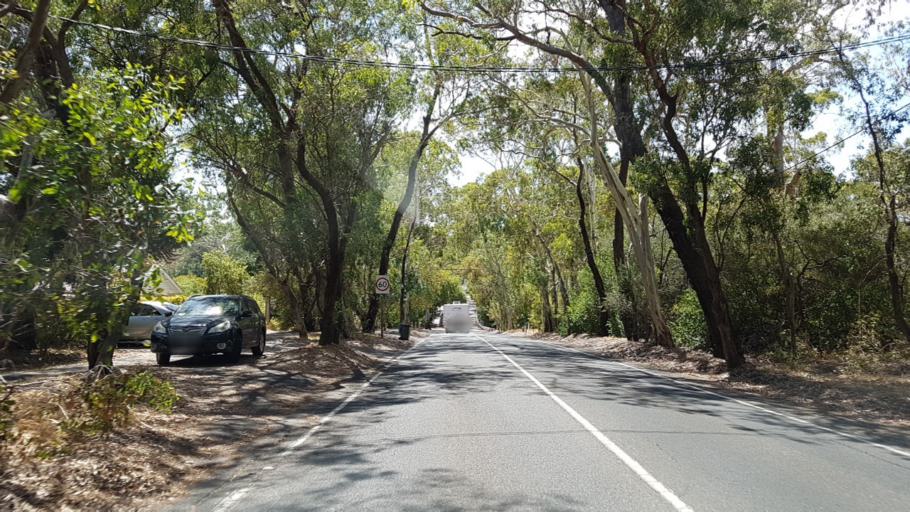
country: AU
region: South Australia
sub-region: Mitcham
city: Belair
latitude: -35.0111
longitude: 138.6334
